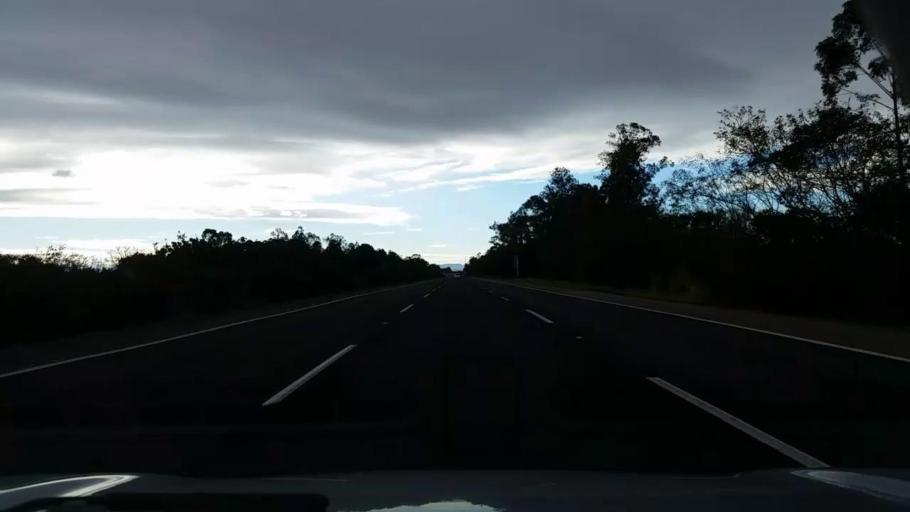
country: BR
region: Rio Grande do Sul
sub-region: Taquara
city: Taquara
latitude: -29.8902
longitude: -50.7031
